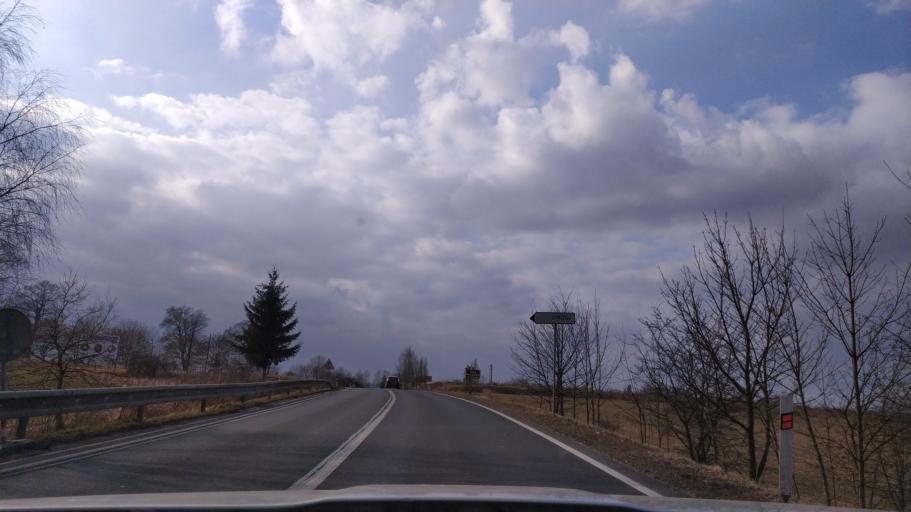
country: CZ
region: Karlovarsky
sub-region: Okres Cheb
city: Frantiskovy Lazne
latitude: 50.1069
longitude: 12.3621
